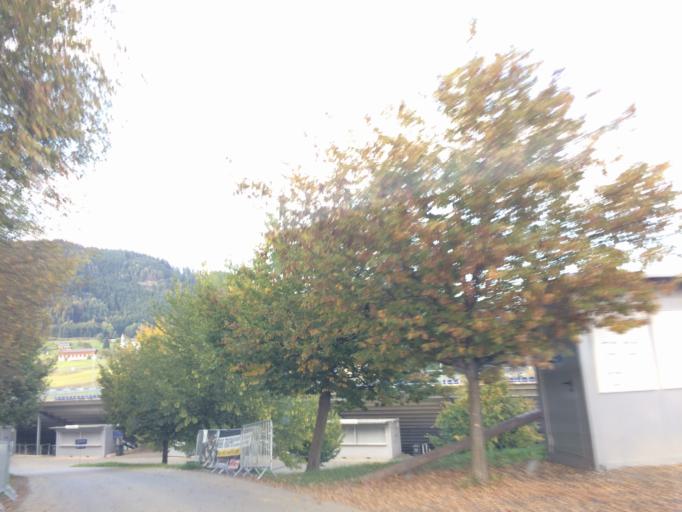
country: AT
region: Styria
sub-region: Politischer Bezirk Murtal
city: Flatschach
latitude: 47.2196
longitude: 14.7586
